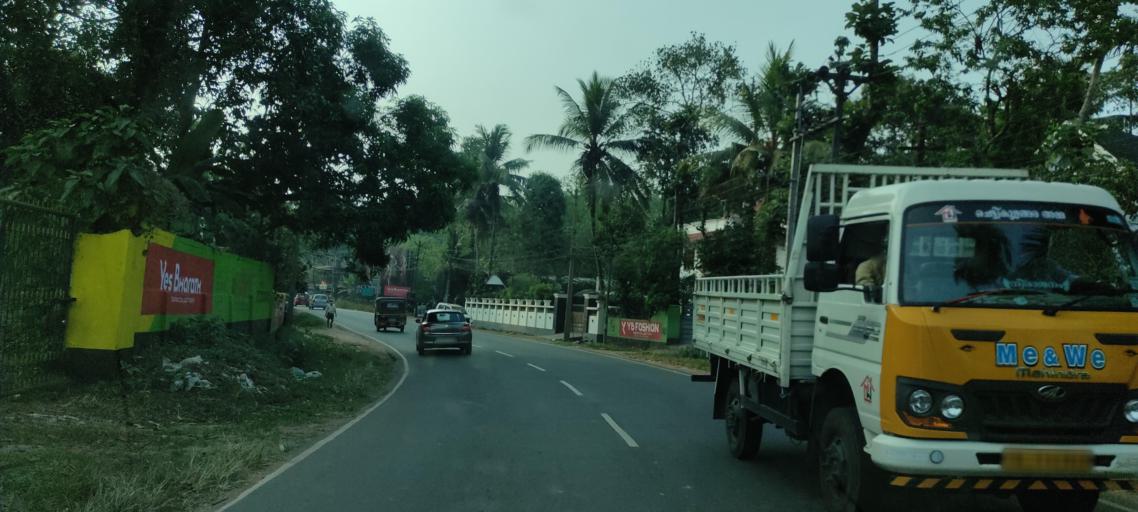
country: IN
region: Kerala
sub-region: Pattanamtitta
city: Adur
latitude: 9.1671
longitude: 76.6790
